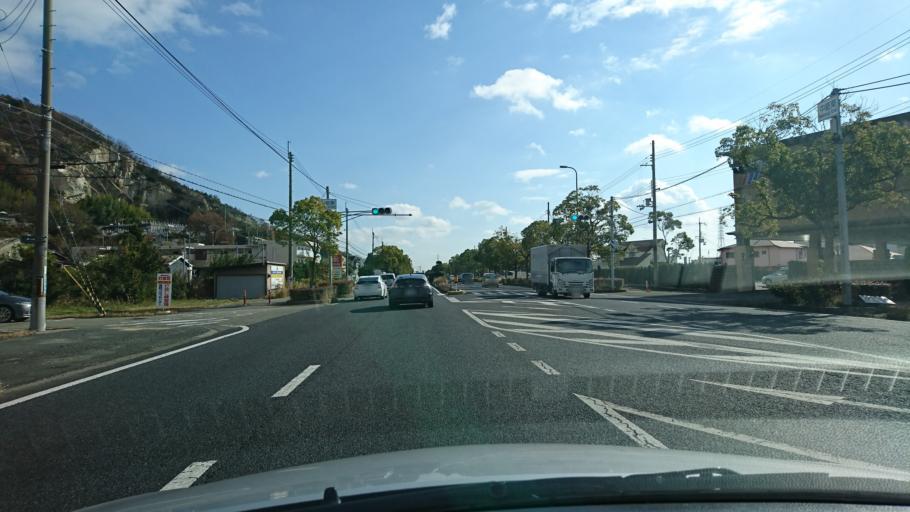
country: JP
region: Hyogo
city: Kakogawacho-honmachi
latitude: 34.7827
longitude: 134.7859
